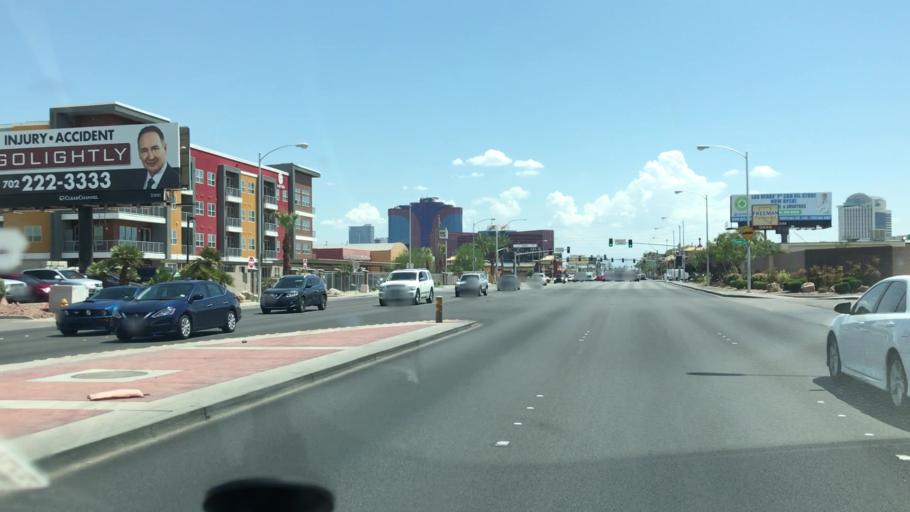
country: US
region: Nevada
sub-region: Clark County
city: Paradise
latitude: 36.1288
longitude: -115.1903
